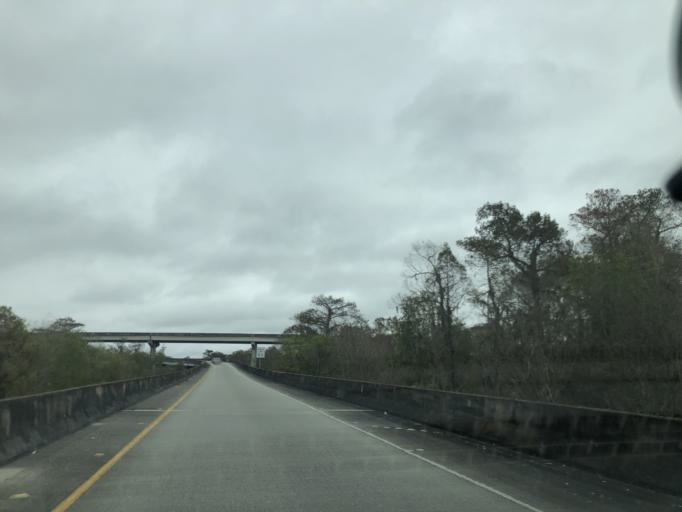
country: US
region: Louisiana
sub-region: Saint Charles Parish
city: Saint Rose
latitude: 29.9757
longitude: -90.3239
